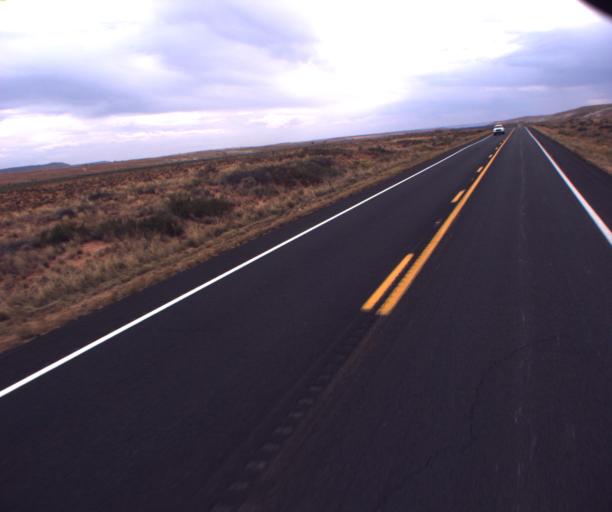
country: US
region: Arizona
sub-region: Coconino County
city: Kaibito
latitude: 36.3600
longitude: -110.9032
